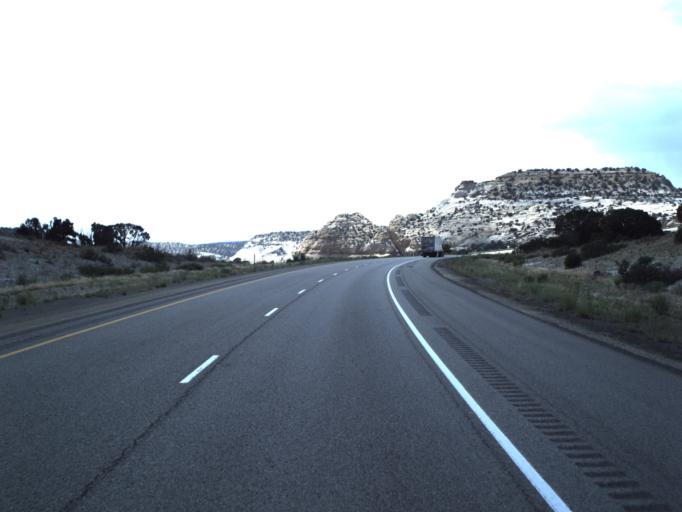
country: US
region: Utah
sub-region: Emery County
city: Ferron
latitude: 38.8481
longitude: -110.8883
